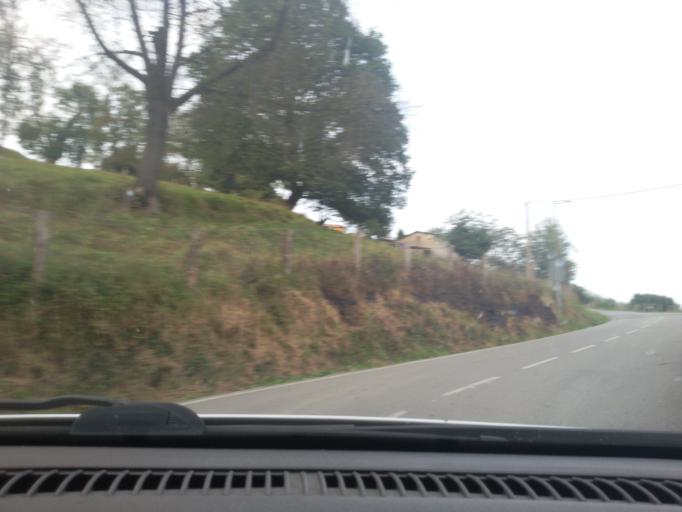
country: ES
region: Asturias
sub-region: Province of Asturias
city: Bimenes
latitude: 43.3366
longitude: -5.5858
